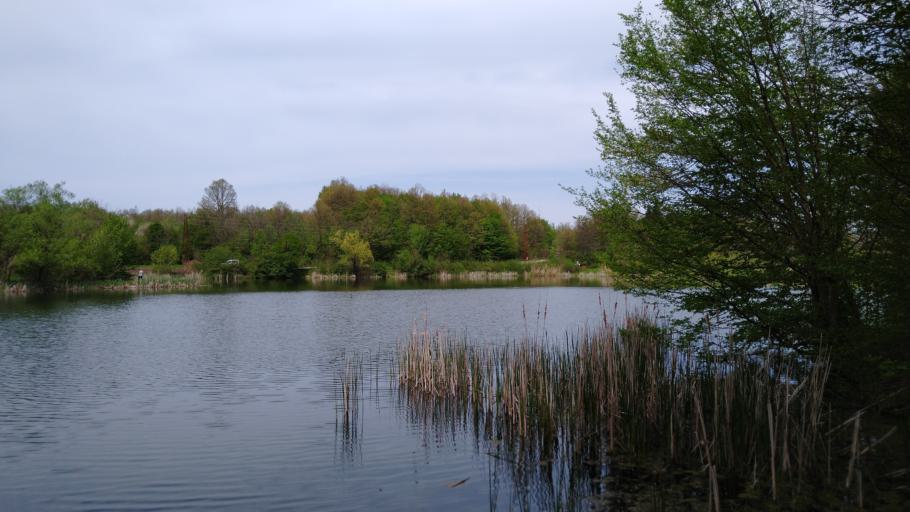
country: BG
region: Gabrovo
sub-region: Obshtina Gabrovo
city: Gabrovo
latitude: 42.8930
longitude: 25.2695
